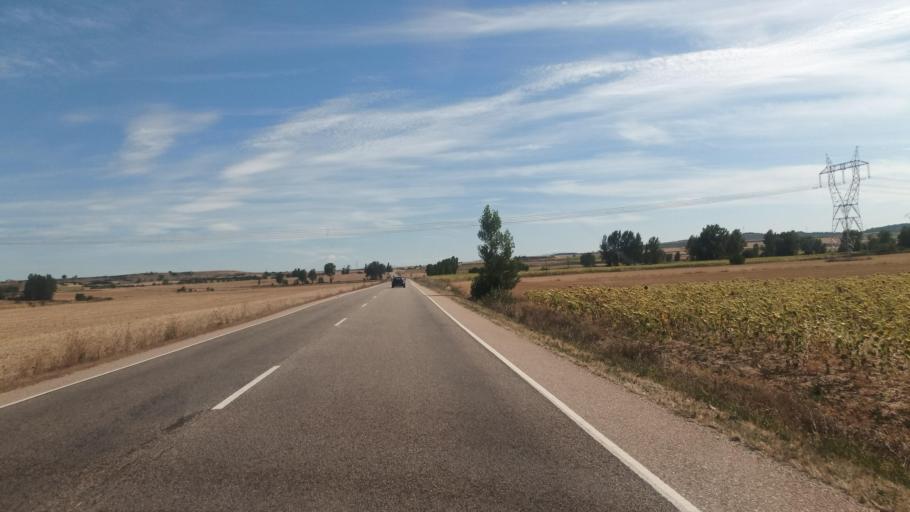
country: ES
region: Castille and Leon
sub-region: Provincia de Burgos
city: Aguilar de Bureba
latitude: 42.5930
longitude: -3.3436
